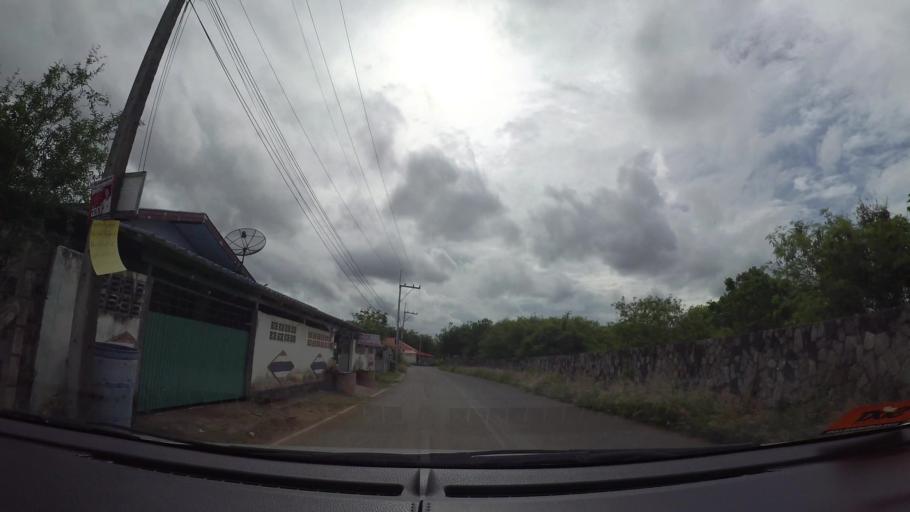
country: TH
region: Chon Buri
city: Sattahip
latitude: 12.7193
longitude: 100.9098
